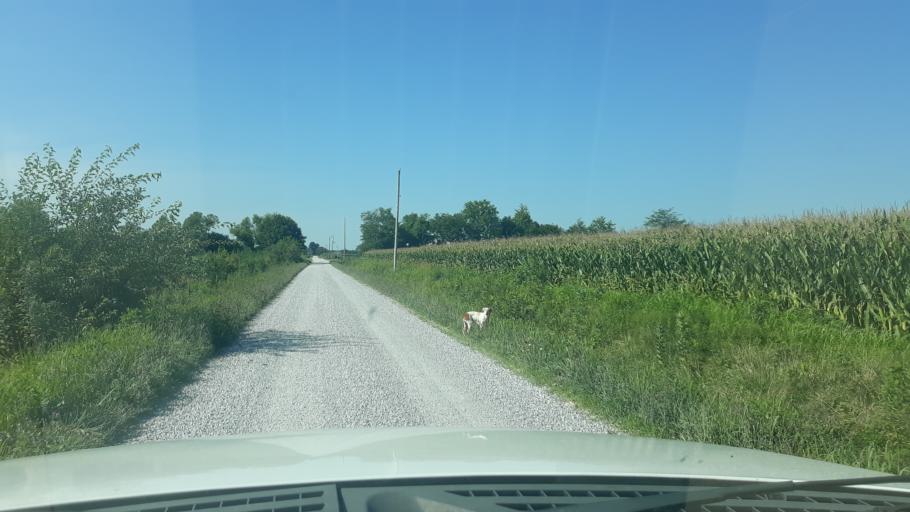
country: US
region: Illinois
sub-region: Saline County
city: Eldorado
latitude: 37.8494
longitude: -88.4849
